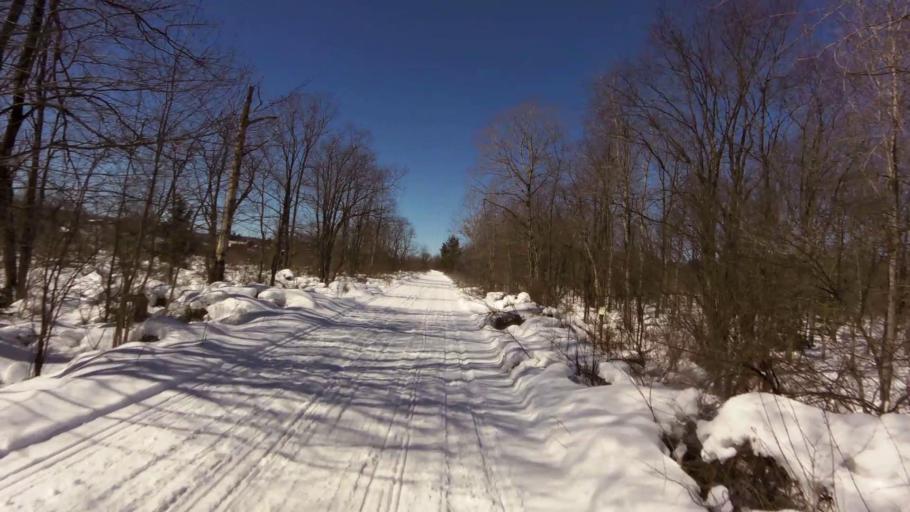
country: US
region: New York
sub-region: Cattaraugus County
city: Franklinville
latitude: 42.4242
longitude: -78.3774
